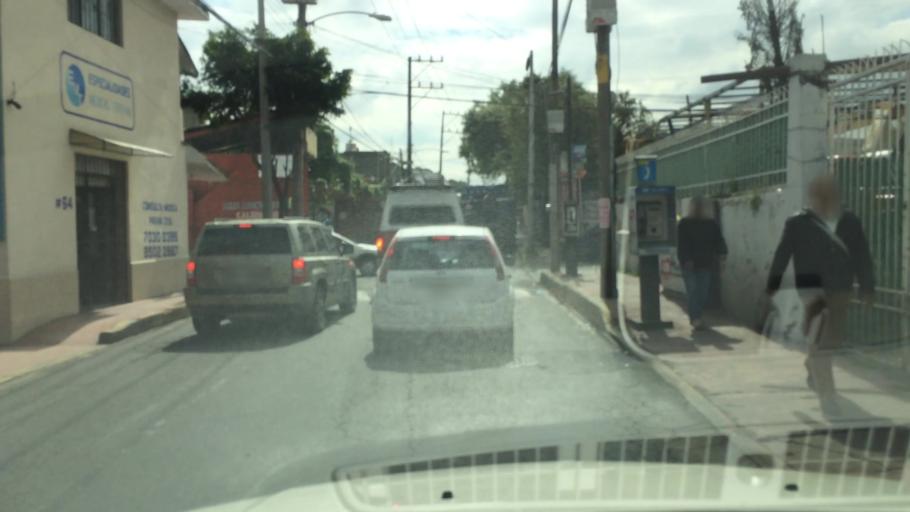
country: MX
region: Mexico City
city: Tlalpan
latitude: 19.2797
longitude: -99.1359
